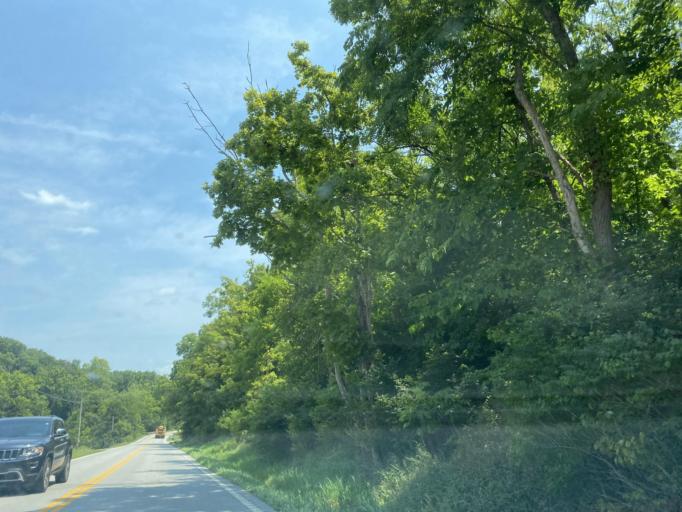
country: US
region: Kentucky
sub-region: Campbell County
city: Claryville
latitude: 38.9267
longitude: -84.4346
